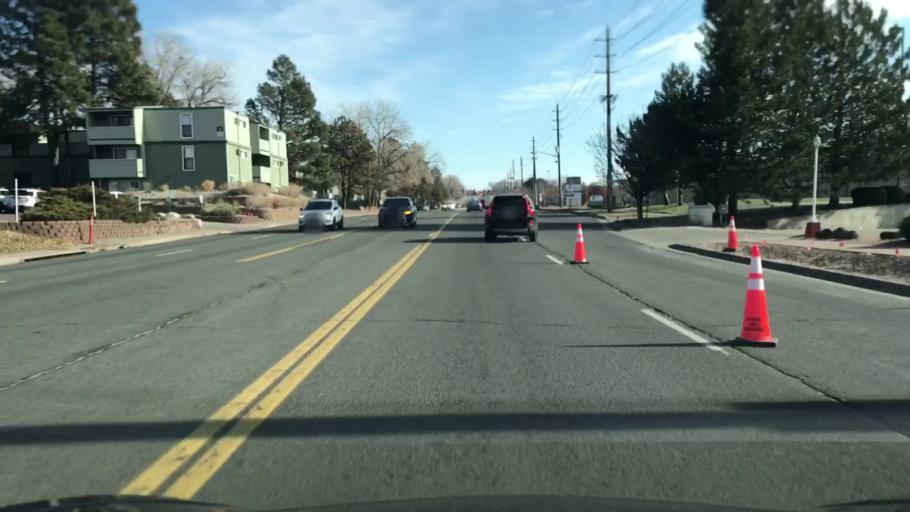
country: US
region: Colorado
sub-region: Arapahoe County
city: Glendale
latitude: 39.6999
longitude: -104.9074
